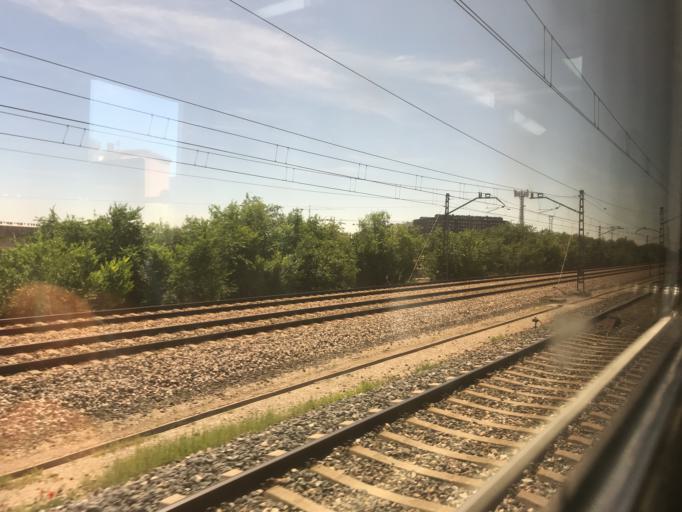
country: ES
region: Madrid
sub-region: Provincia de Madrid
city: Villaverde
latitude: 40.3459
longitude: -3.6839
